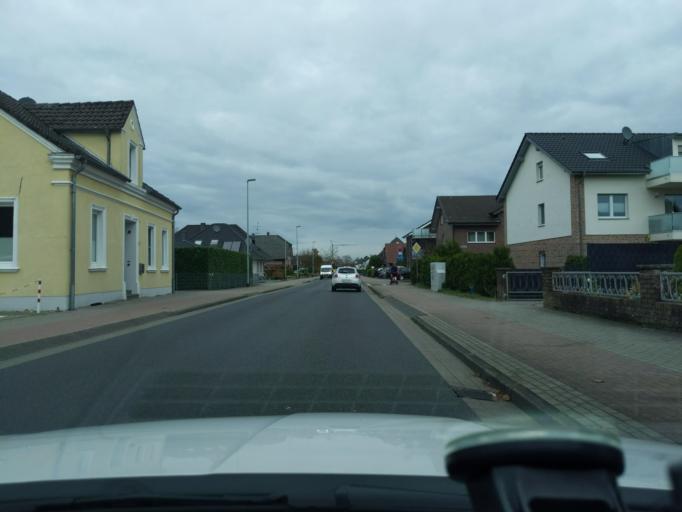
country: DE
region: North Rhine-Westphalia
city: Rees
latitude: 51.7694
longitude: 6.4008
